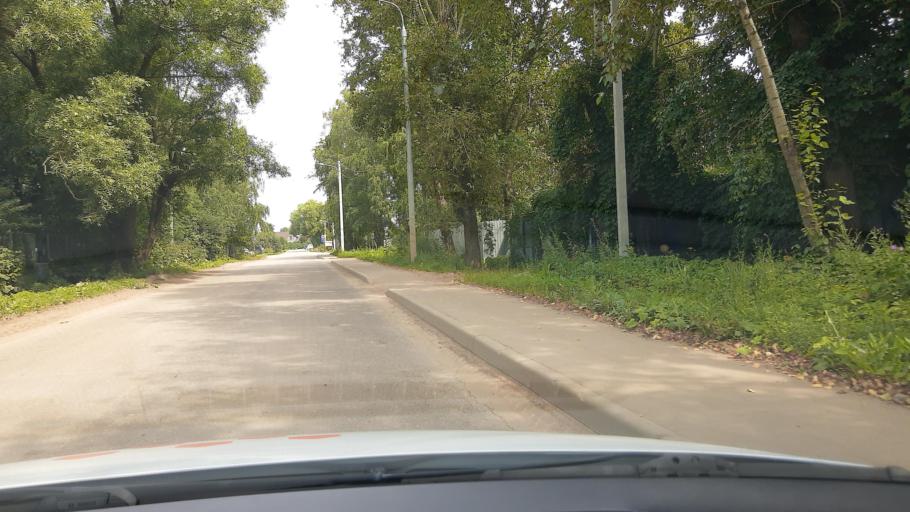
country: RU
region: Moskovskaya
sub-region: Leninskiy Rayon
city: Molokovo
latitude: 55.5818
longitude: 37.8439
